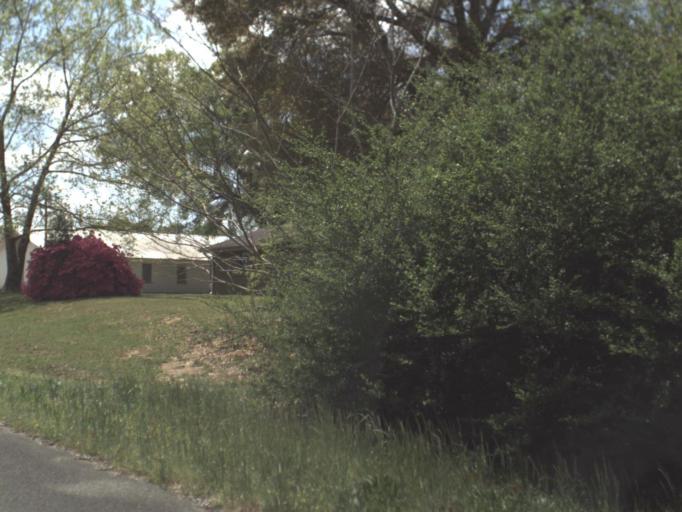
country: US
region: Florida
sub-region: Okaloosa County
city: Crestview
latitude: 30.8563
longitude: -86.6748
